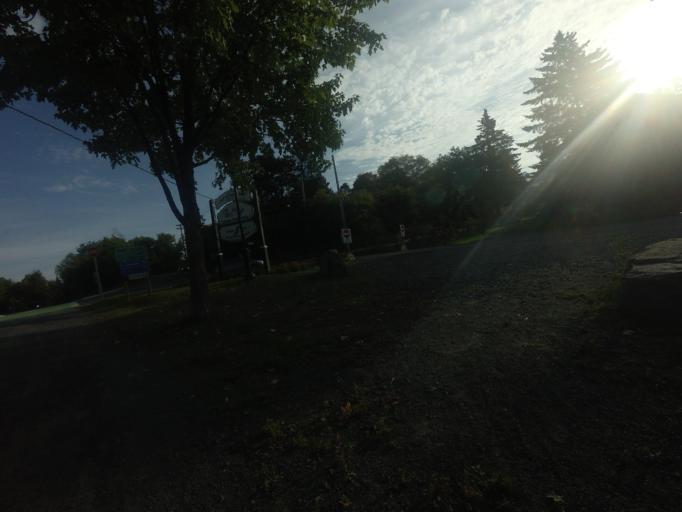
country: CA
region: Quebec
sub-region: Laurentides
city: Sainte-Adele
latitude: 45.9406
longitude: -74.1191
